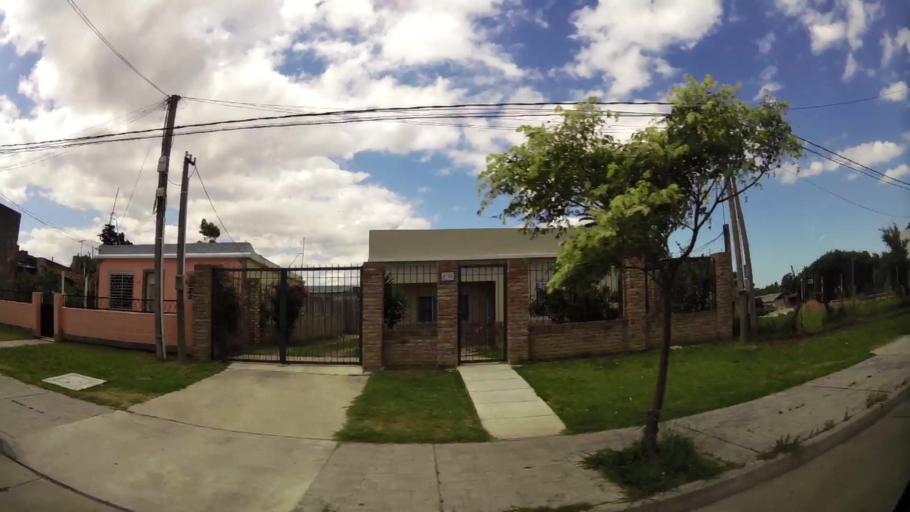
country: UY
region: Canelones
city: La Paz
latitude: -34.8399
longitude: -56.2485
